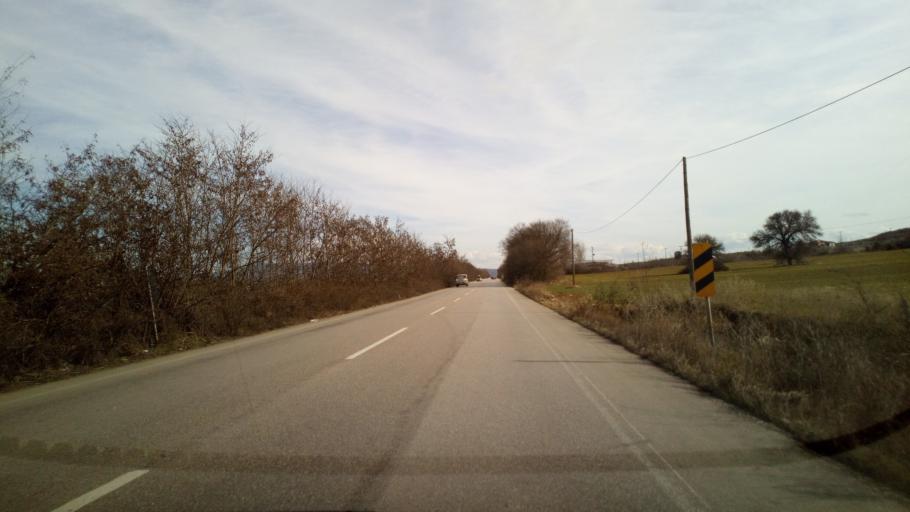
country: GR
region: Central Macedonia
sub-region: Nomos Thessalonikis
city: Agios Vasileios
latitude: 40.6545
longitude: 23.1582
